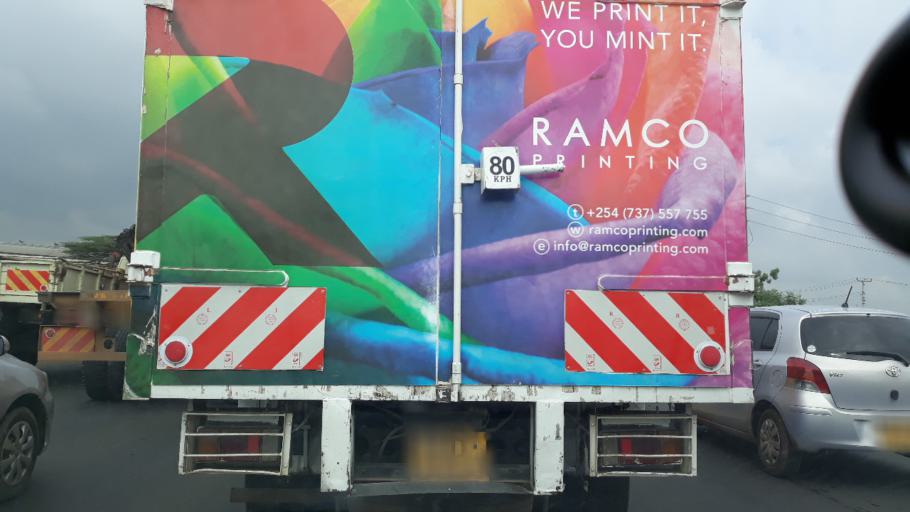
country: KE
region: Nairobi Area
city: Pumwani
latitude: -1.3309
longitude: 36.8871
